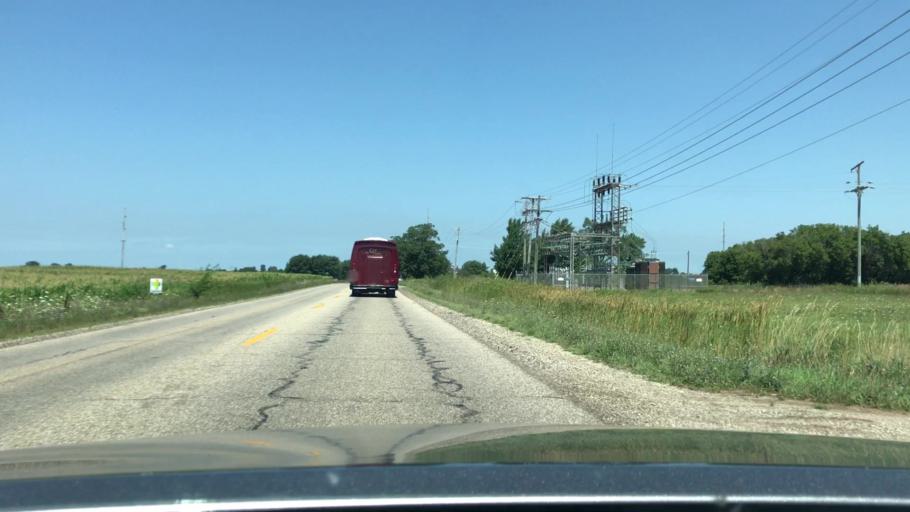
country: US
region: Michigan
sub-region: Ottawa County
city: Zeeland
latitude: 42.8683
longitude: -86.0797
